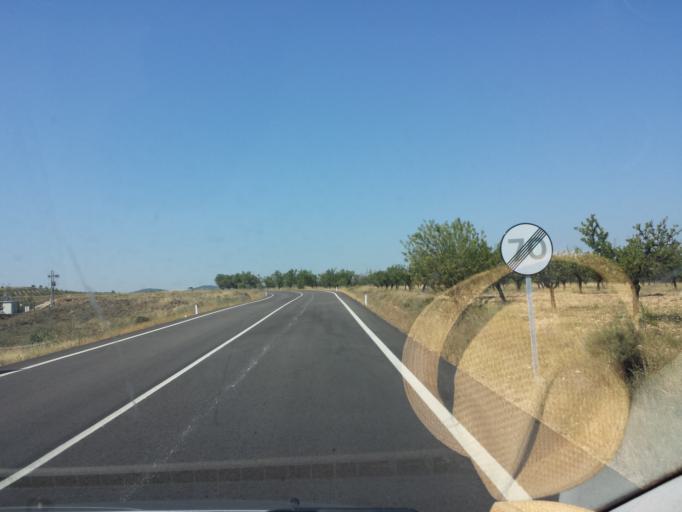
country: ES
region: Aragon
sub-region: Provincia de Zaragoza
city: Paracuellos de Jiloca
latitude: 41.3111
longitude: -1.6706
